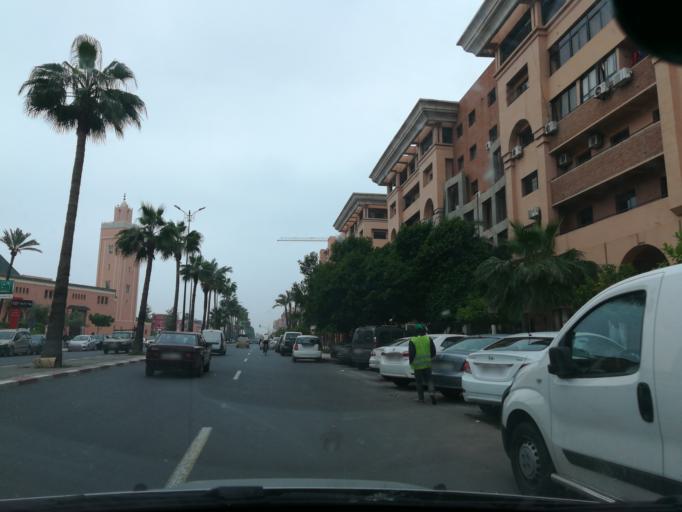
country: MA
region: Marrakech-Tensift-Al Haouz
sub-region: Marrakech
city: Marrakesh
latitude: 31.6578
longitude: -8.0050
